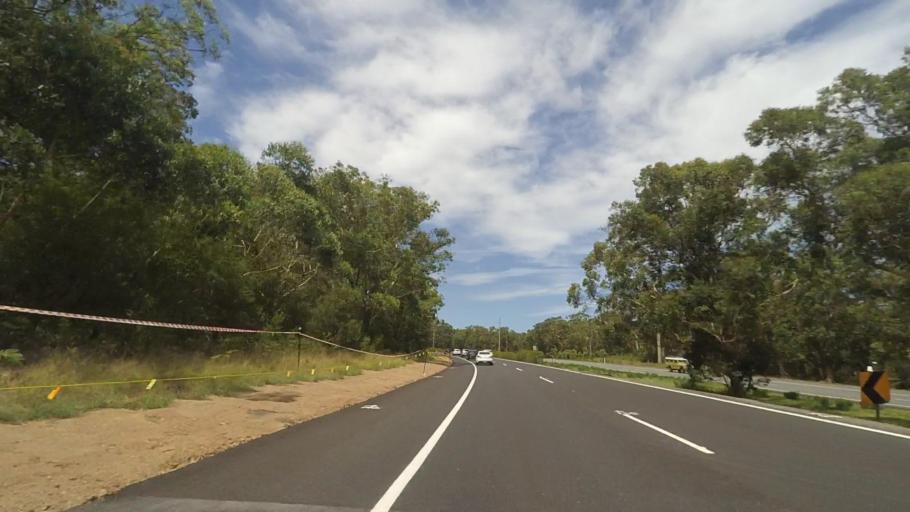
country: AU
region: New South Wales
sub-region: Port Stephens Shire
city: Anna Bay
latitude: -32.7789
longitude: 152.0008
